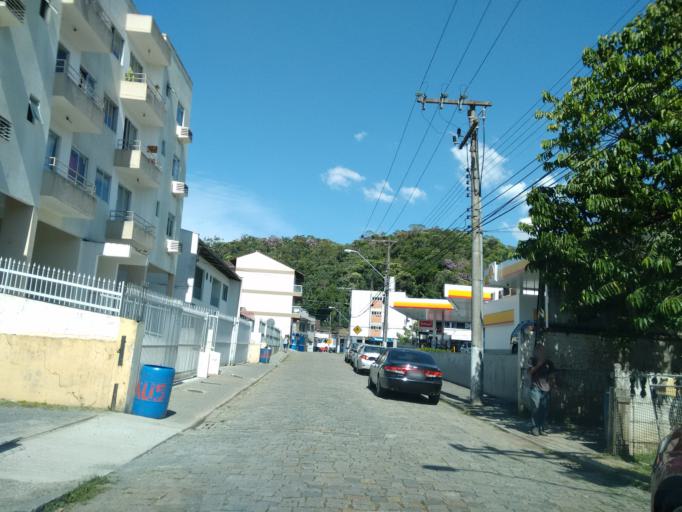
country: BR
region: Santa Catarina
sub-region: Blumenau
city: Blumenau
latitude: -26.9307
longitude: -49.0603
